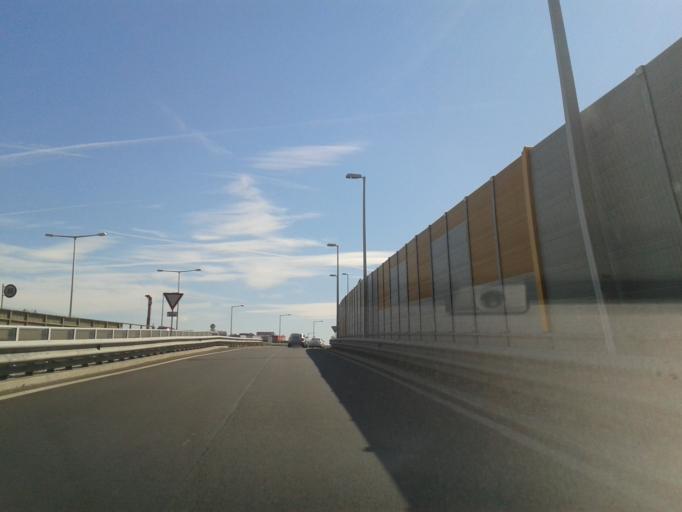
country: AT
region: Lower Austria
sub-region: Politischer Bezirk Modling
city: Vosendorf
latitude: 48.1498
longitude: 16.3366
